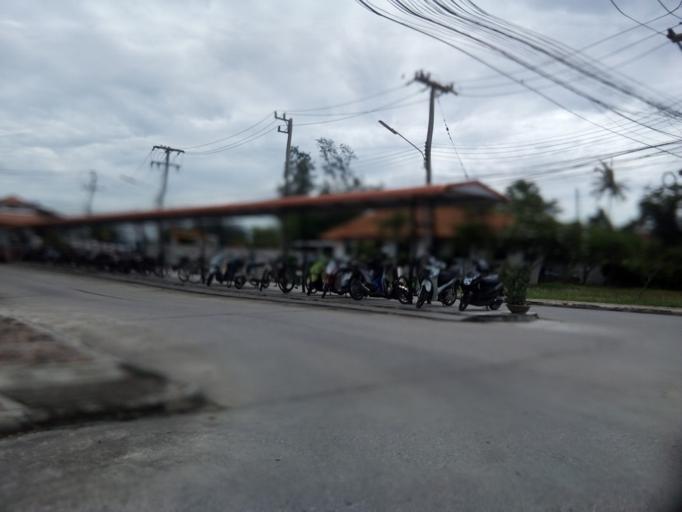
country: TH
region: Pathum Thani
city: Nong Suea
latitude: 14.0552
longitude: 100.8352
